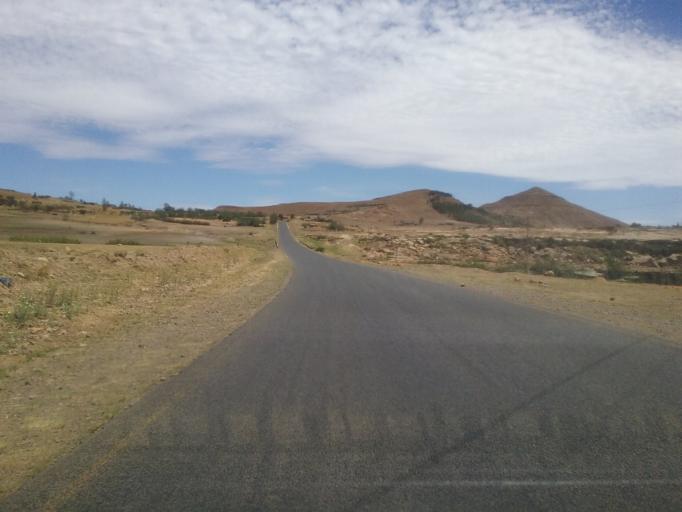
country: LS
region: Mafeteng
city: Mafeteng
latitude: -29.9239
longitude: 27.2555
